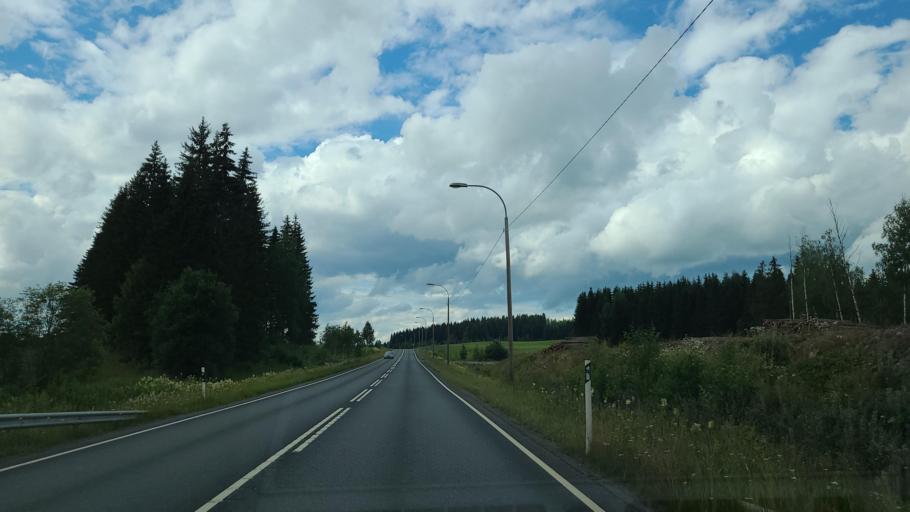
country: FI
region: Northern Savo
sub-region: Kuopio
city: Nilsiae
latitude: 63.1346
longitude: 28.0217
